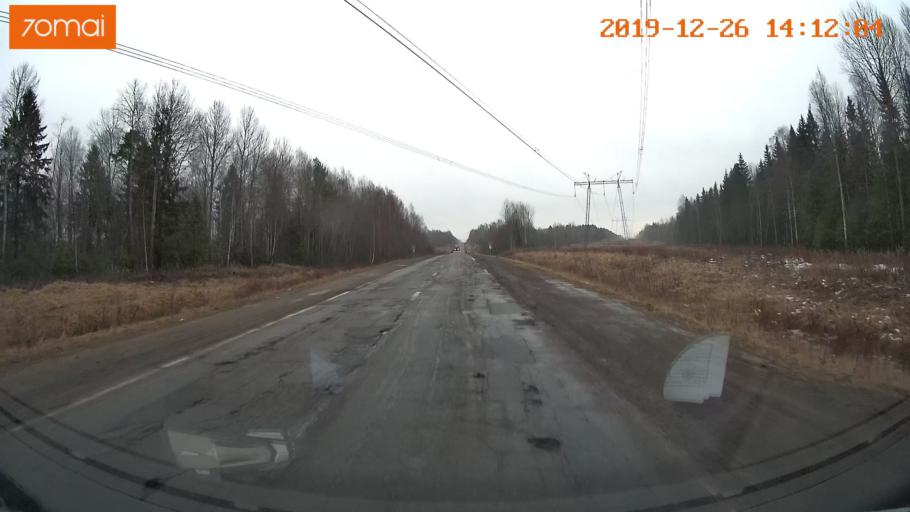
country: RU
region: Jaroslavl
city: Poshekhon'ye
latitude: 58.5106
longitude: 38.9843
